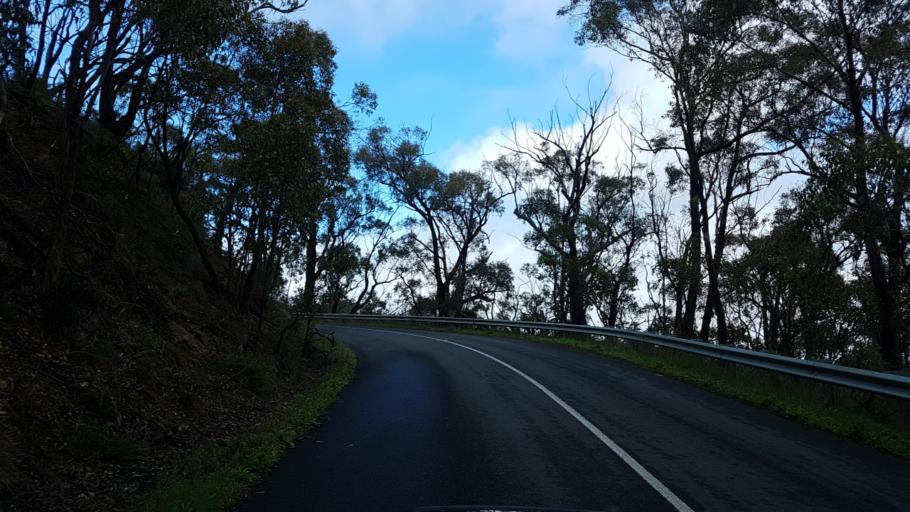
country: AU
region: South Australia
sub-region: Adelaide Hills
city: Adelaide Hills
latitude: -34.9079
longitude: 138.7627
